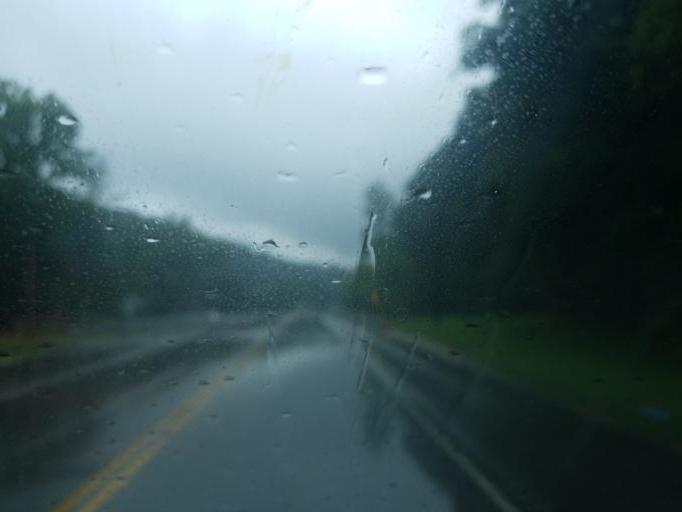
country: US
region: Kentucky
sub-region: Rowan County
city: Morehead
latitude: 38.2473
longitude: -83.3431
